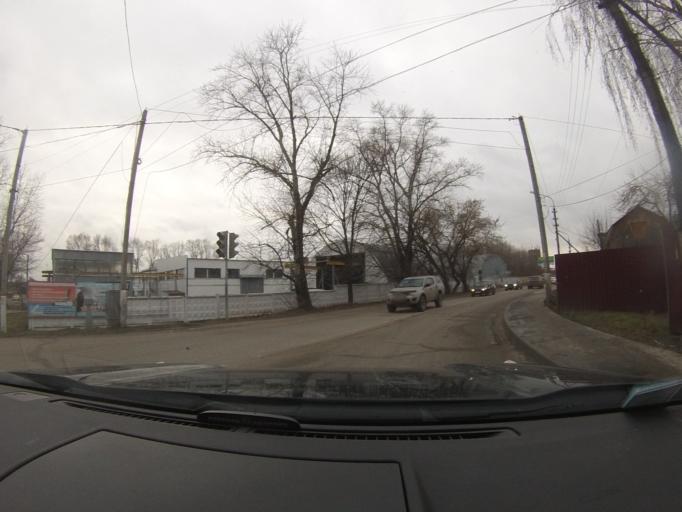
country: RU
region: Moskovskaya
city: Lopatinskiy
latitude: 55.3270
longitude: 38.7117
